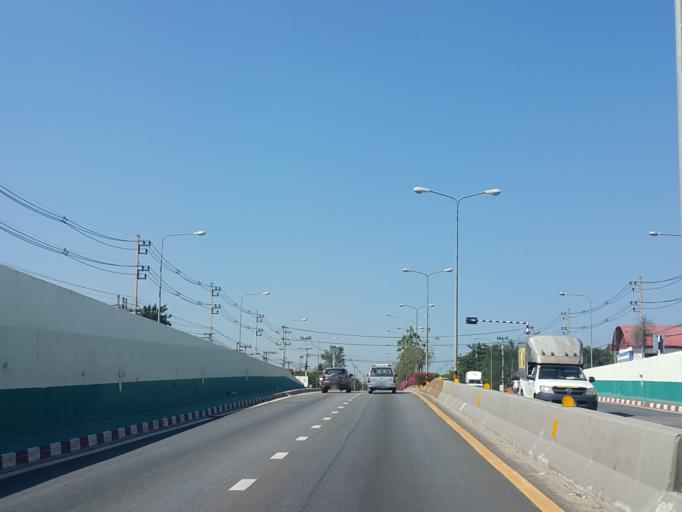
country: TH
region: Chiang Mai
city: San Sai
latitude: 18.8104
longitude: 99.0255
